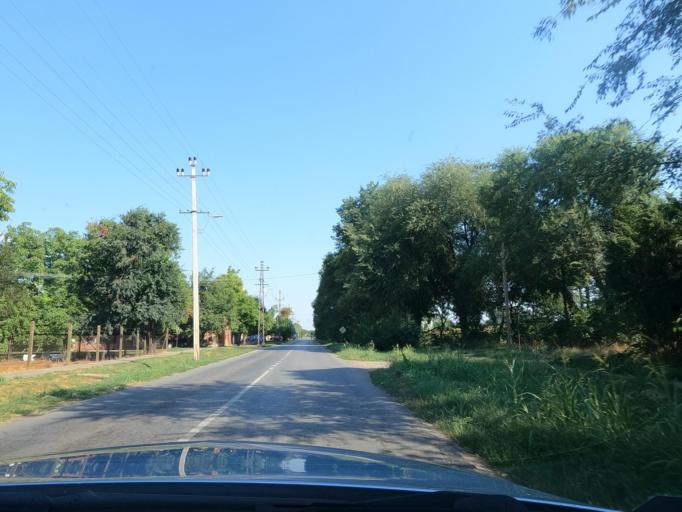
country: RS
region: Autonomna Pokrajina Vojvodina
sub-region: Juznobacki Okrug
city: Becej
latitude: 45.6287
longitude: 20.0214
